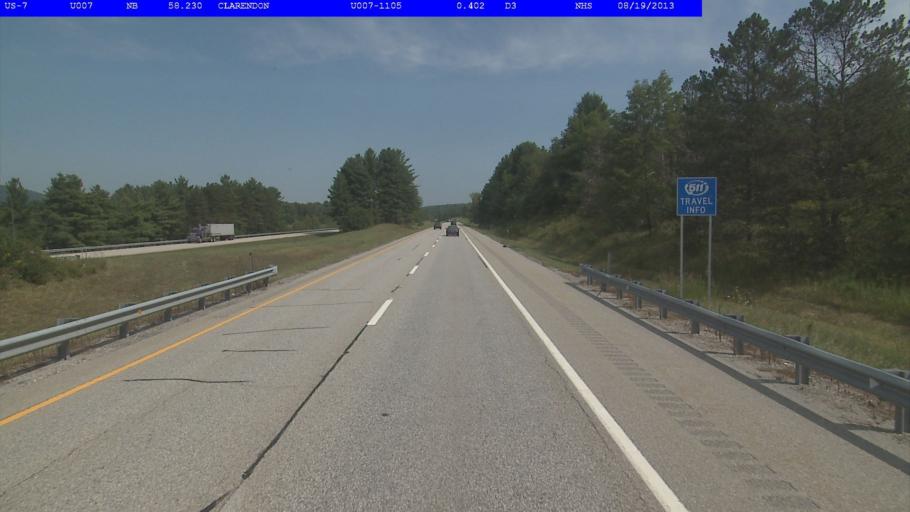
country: US
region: Vermont
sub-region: Rutland County
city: Rutland
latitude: 43.4998
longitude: -72.9680
